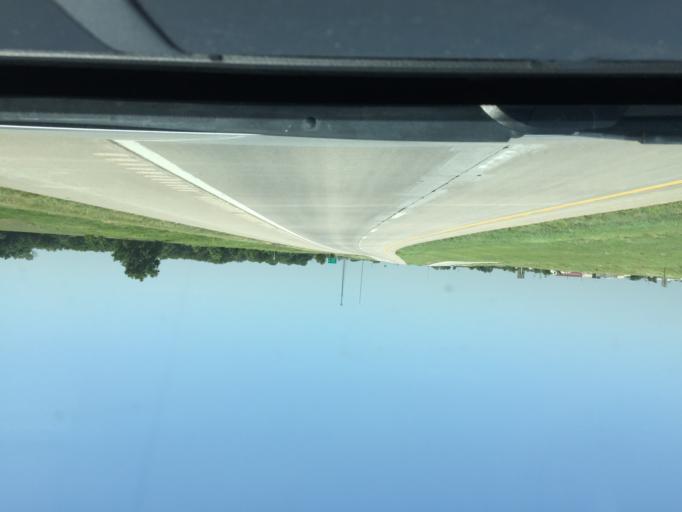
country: US
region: Kansas
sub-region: Reno County
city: Haven
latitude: 37.9367
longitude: -97.8752
